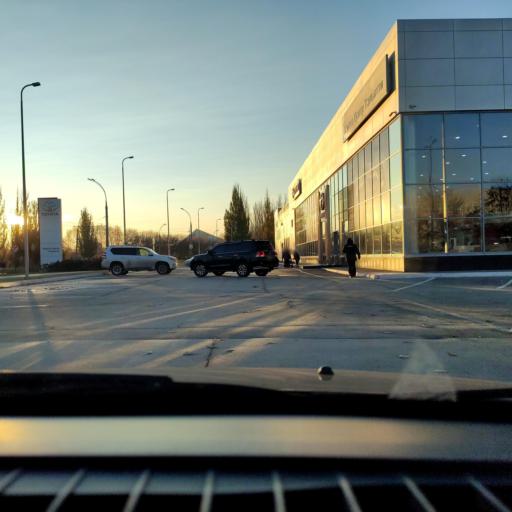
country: RU
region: Samara
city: Tol'yatti
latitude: 53.5445
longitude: 49.2769
